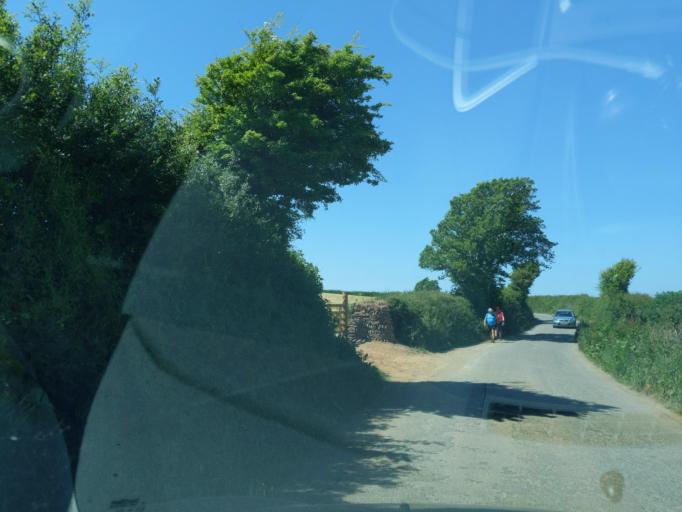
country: GB
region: England
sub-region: Cornwall
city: Wadebridge
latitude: 50.5767
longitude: -4.8305
